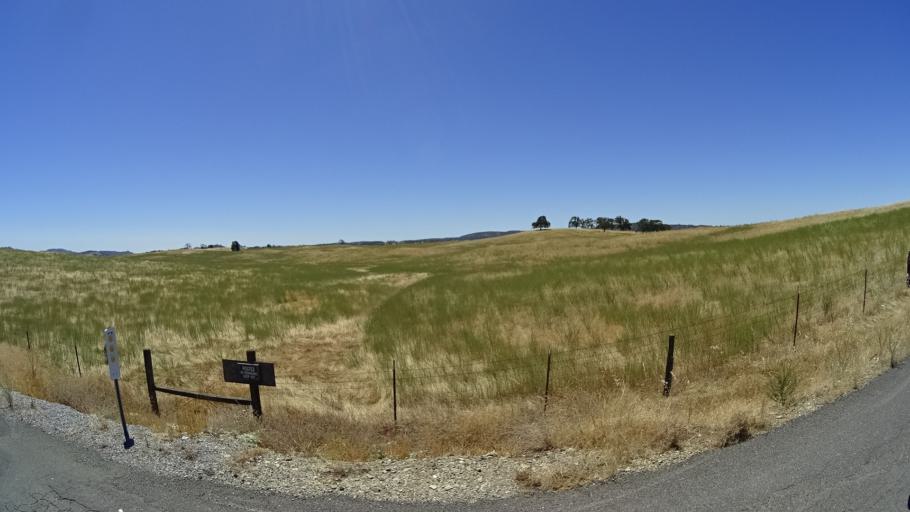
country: US
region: California
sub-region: Calaveras County
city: Copperopolis
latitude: 38.0537
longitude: -120.7377
